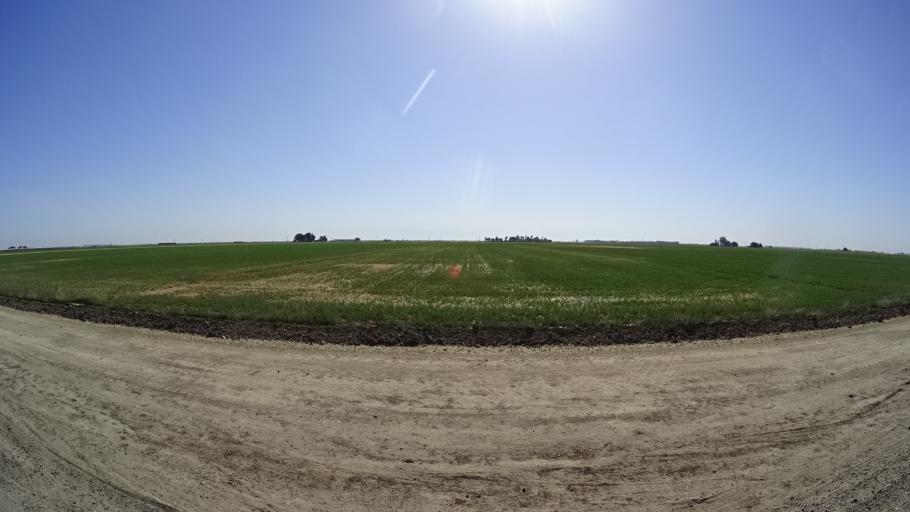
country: US
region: California
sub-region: Kings County
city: Home Garden
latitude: 36.2335
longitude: -119.5562
